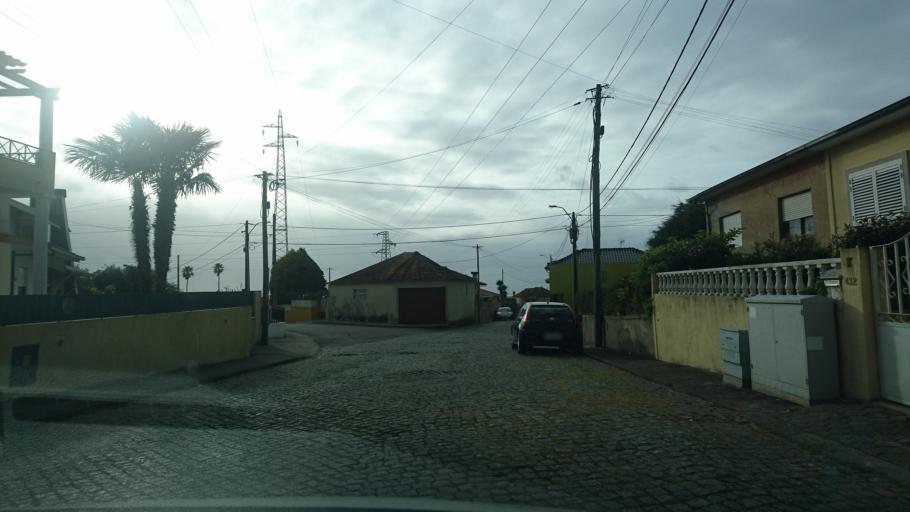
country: PT
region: Aveiro
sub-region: Ovar
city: Esmoriz
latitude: 40.9578
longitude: -8.6202
